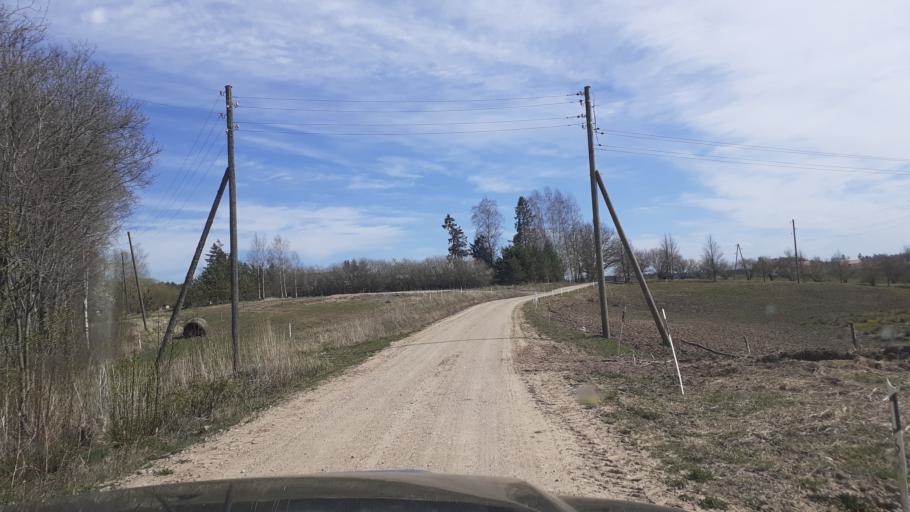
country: LV
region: Kuldigas Rajons
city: Kuldiga
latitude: 56.8373
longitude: 21.9973
